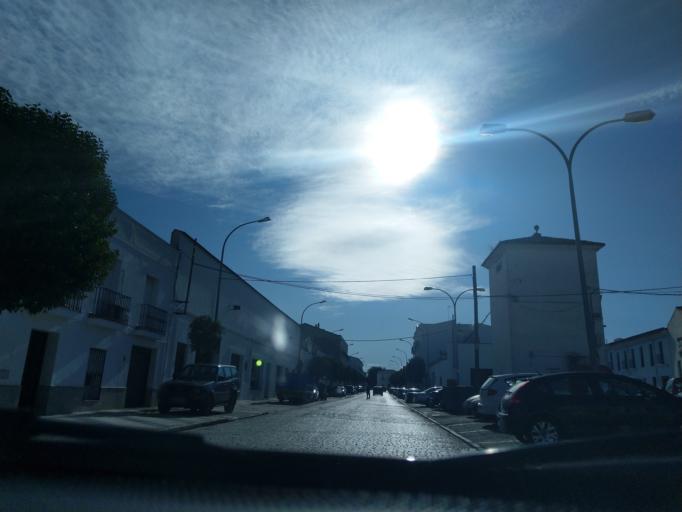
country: ES
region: Extremadura
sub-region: Provincia de Badajoz
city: Llerena
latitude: 38.2387
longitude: -6.0126
